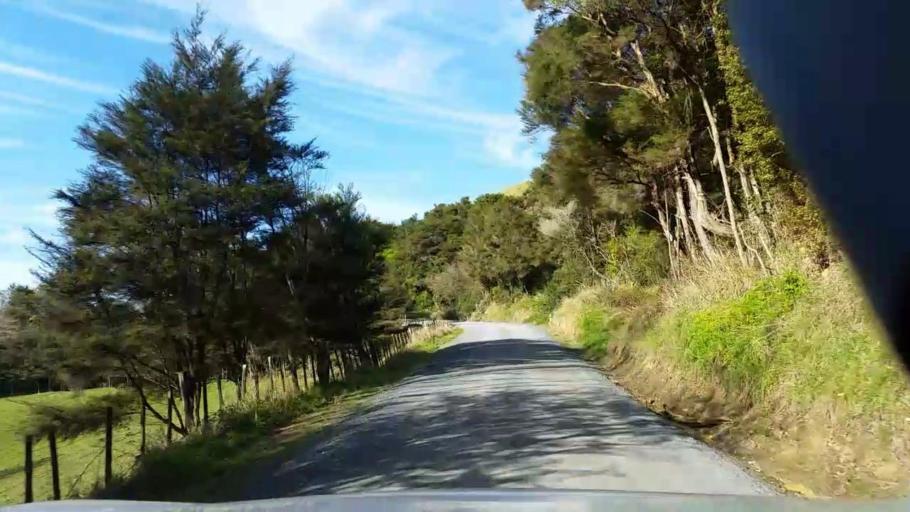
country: NZ
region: Waikato
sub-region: Hauraki District
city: Ngatea
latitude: -37.4760
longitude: 175.4053
